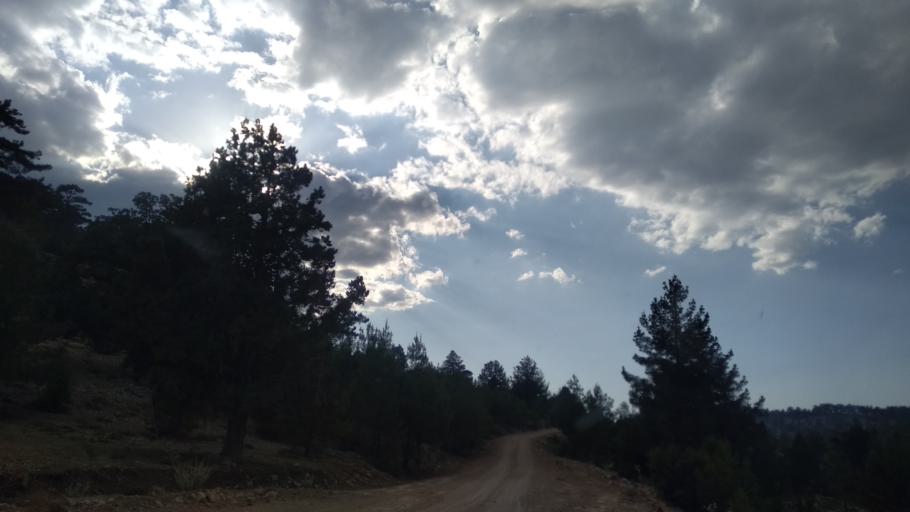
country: TR
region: Mersin
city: Sarikavak
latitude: 36.5960
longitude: 33.7121
